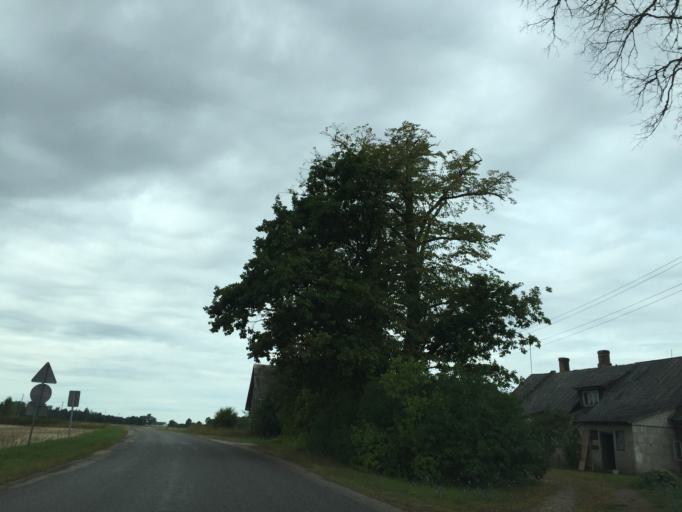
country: LV
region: Engure
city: Smarde
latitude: 56.8034
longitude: 23.2979
